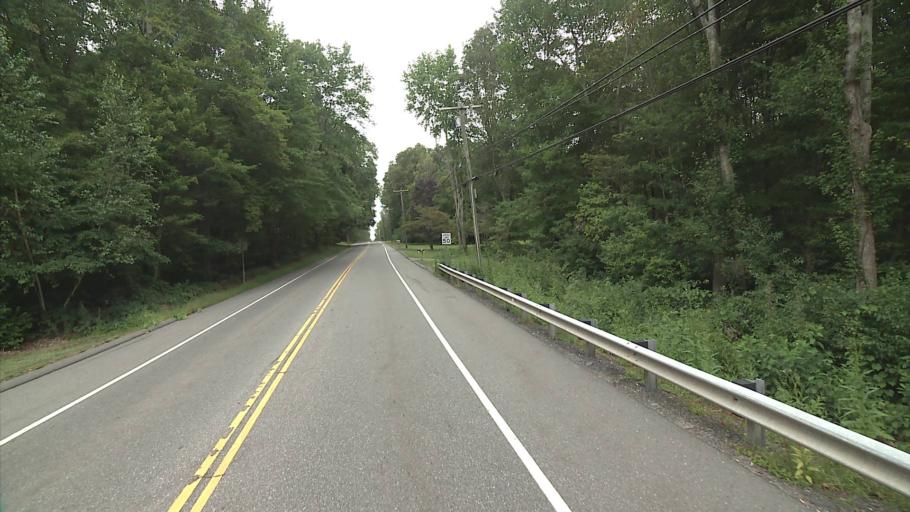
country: US
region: Connecticut
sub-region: New London County
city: Colchester
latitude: 41.6010
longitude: -72.3435
